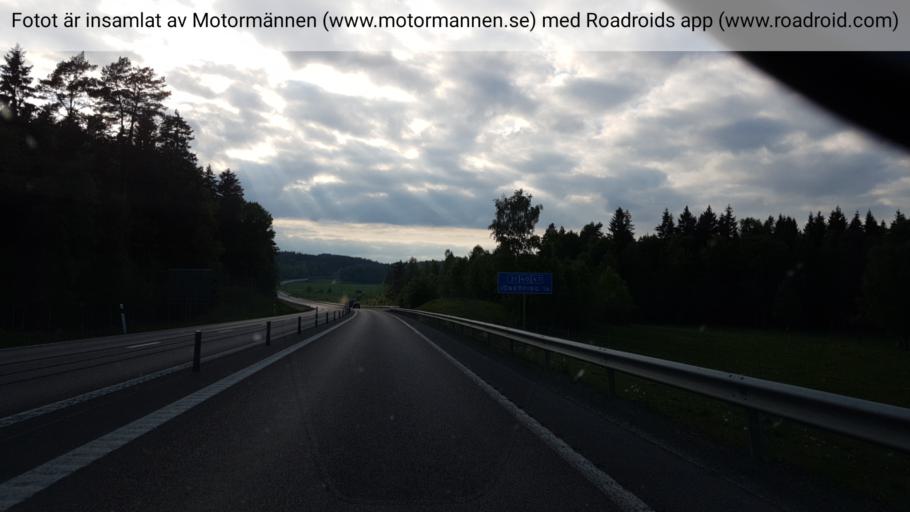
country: SE
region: Joenkoeping
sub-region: Jonkopings Kommun
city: Tenhult
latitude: 57.7189
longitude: 14.3744
